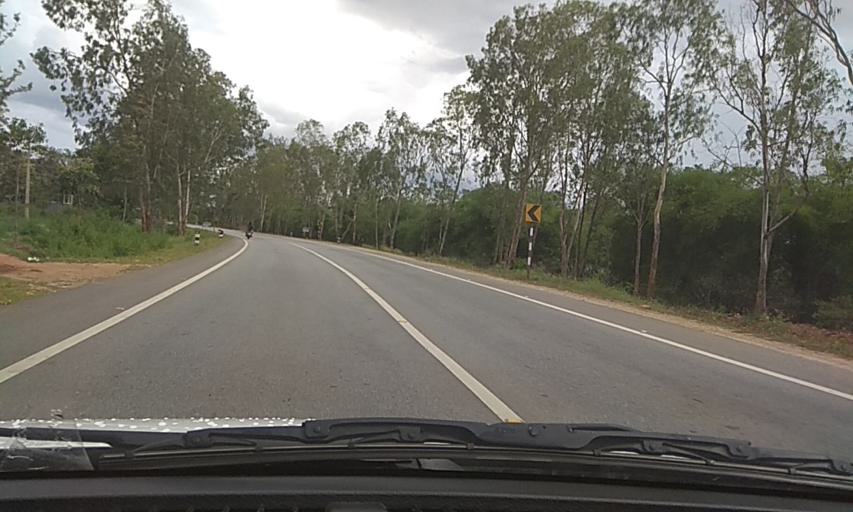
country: IN
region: Karnataka
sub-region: Tumkur
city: Kunigal
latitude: 12.9126
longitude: 77.0328
